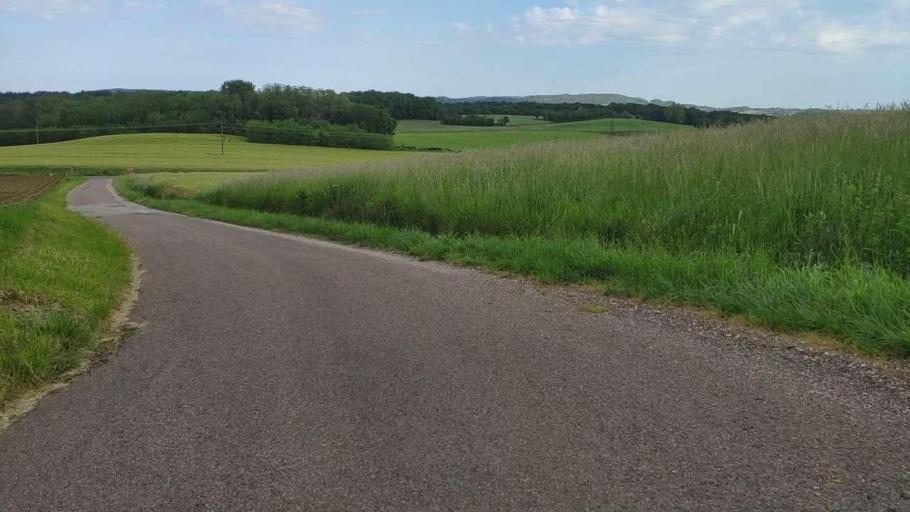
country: FR
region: Franche-Comte
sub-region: Departement du Jura
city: Perrigny
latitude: 46.7414
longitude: 5.6018
